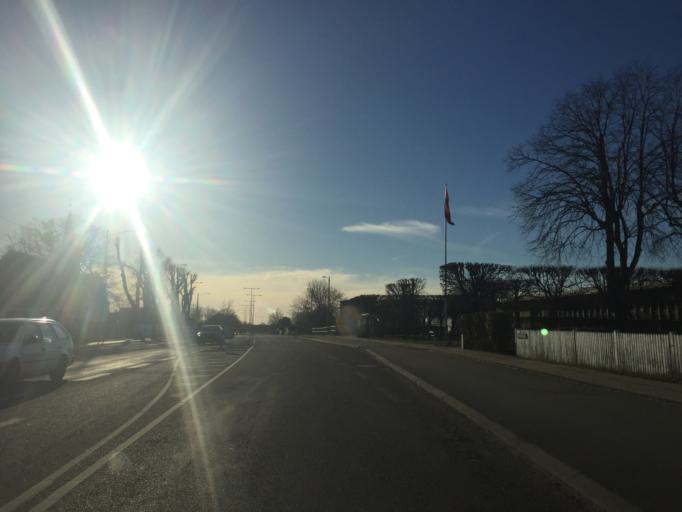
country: DK
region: Capital Region
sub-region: Dragor Kommune
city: Dragor
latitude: 55.5962
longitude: 12.6381
